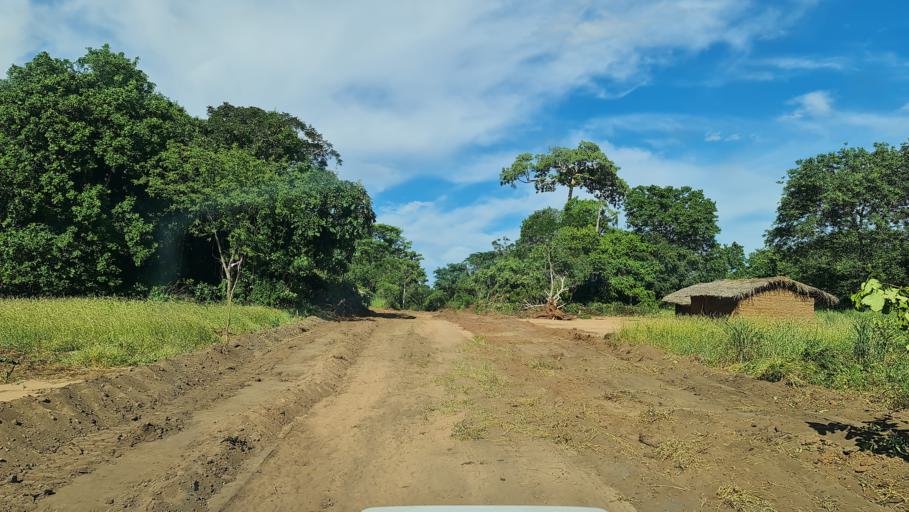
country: MZ
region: Nampula
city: Ilha de Mocambique
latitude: -15.5075
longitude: 40.1444
